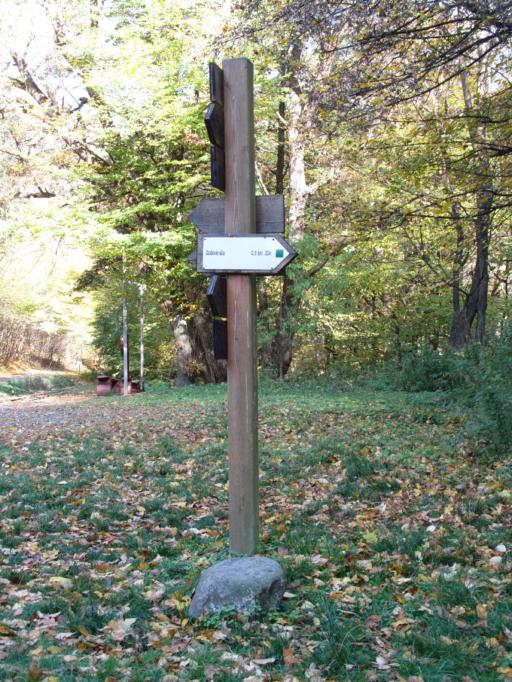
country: SK
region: Nitriansky
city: Sahy
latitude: 47.9831
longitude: 18.8971
